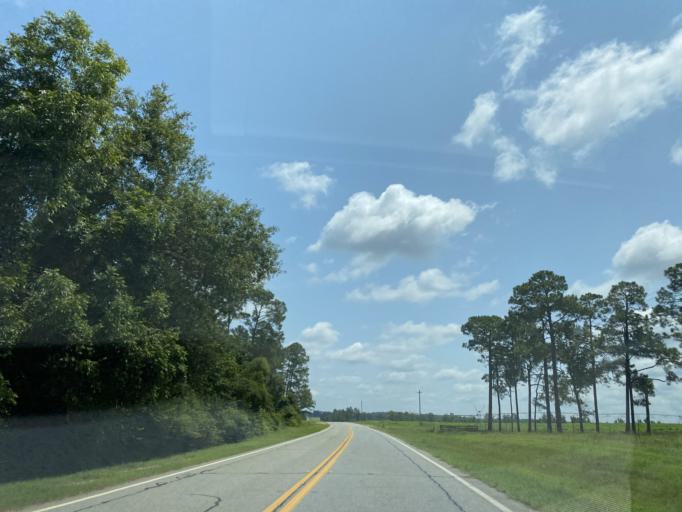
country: US
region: Georgia
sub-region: Wilcox County
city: Abbeville
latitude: 32.0024
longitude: -83.1420
